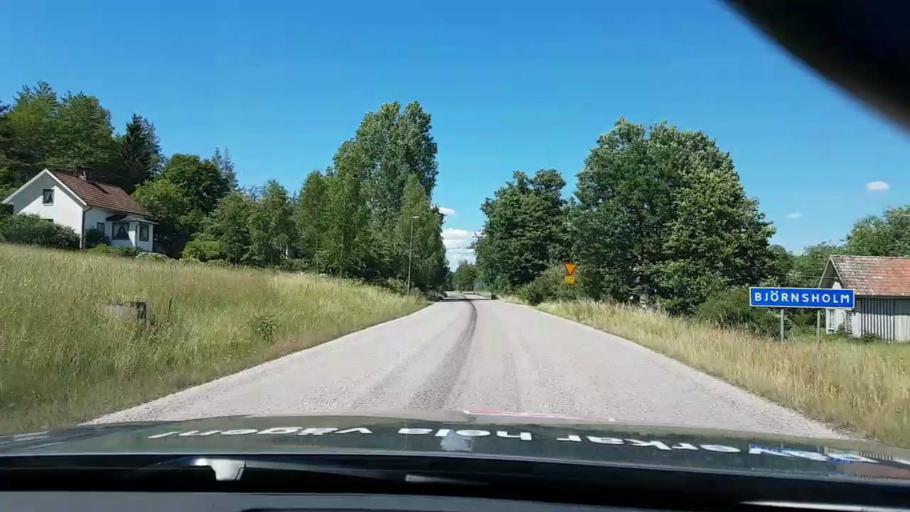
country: SE
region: Kalmar
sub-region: Vasterviks Kommun
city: Forserum
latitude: 57.9491
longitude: 16.4460
